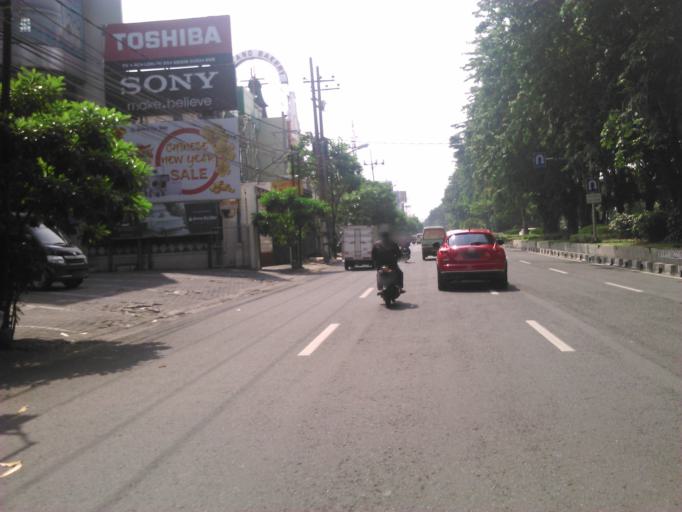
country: ID
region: East Java
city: Gubengairlangga
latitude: -7.2777
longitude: 112.7534
